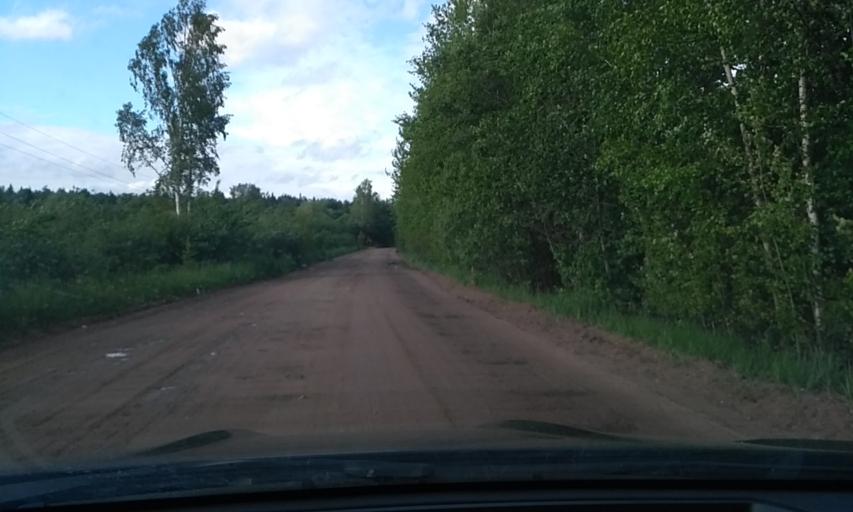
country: RU
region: Leningrad
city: Otradnoye
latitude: 59.8055
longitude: 30.8062
